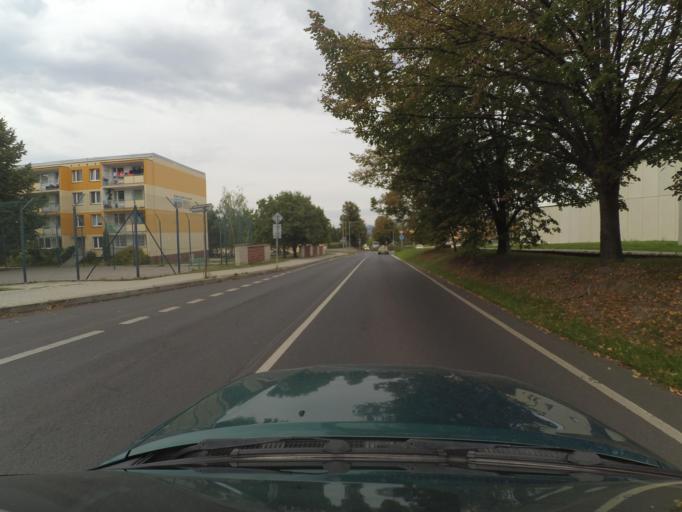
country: CZ
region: Ustecky
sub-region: Okres Louny
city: Louny
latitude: 50.3490
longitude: 13.8058
